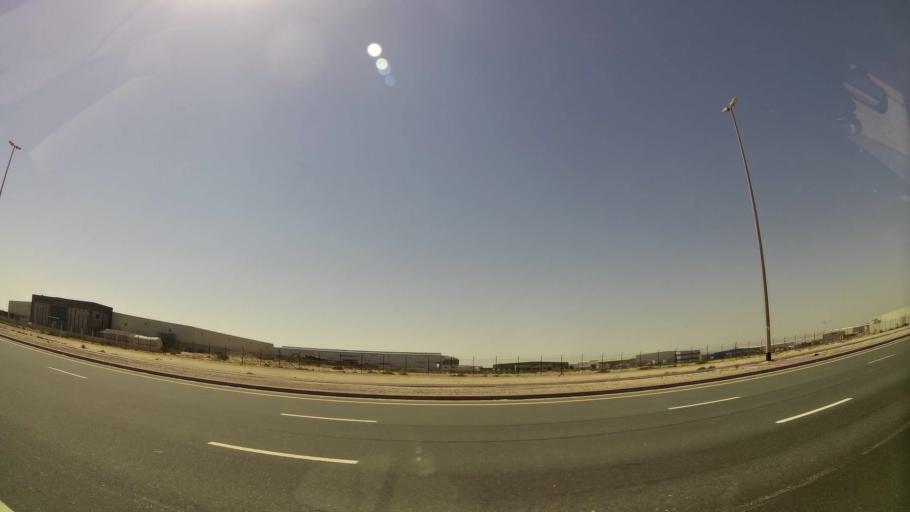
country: AE
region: Dubai
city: Dubai
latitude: 24.9467
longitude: 55.1103
